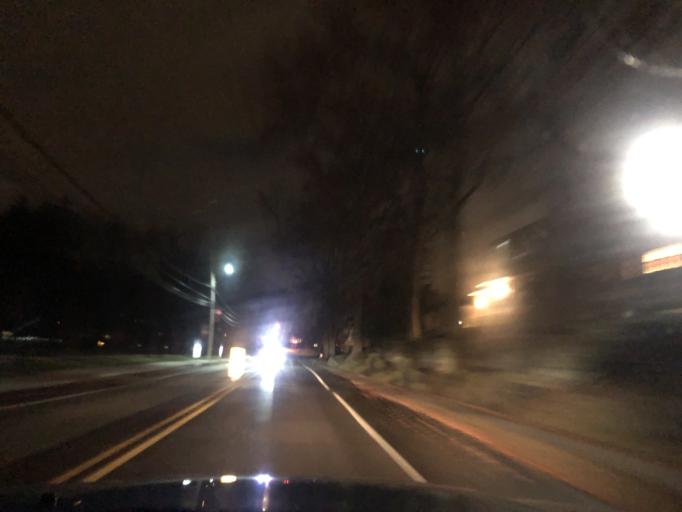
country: US
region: Pennsylvania
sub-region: Delaware County
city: Radnor
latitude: 40.0262
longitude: -75.3406
